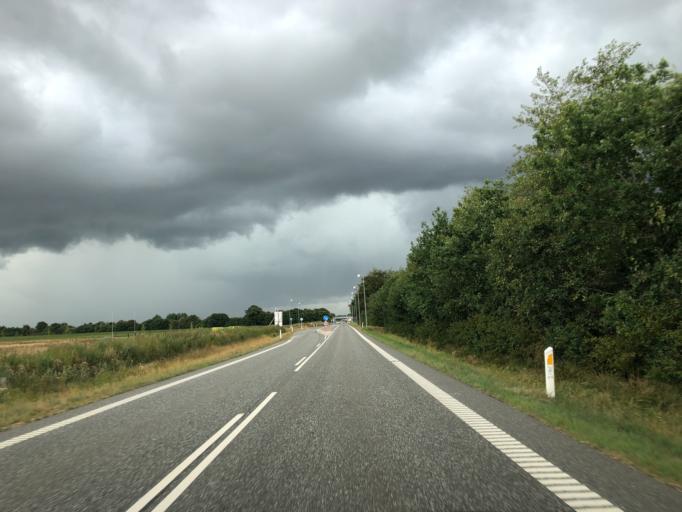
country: DK
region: Central Jutland
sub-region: Ikast-Brande Kommune
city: Bording Kirkeby
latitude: 56.1374
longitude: 9.3606
